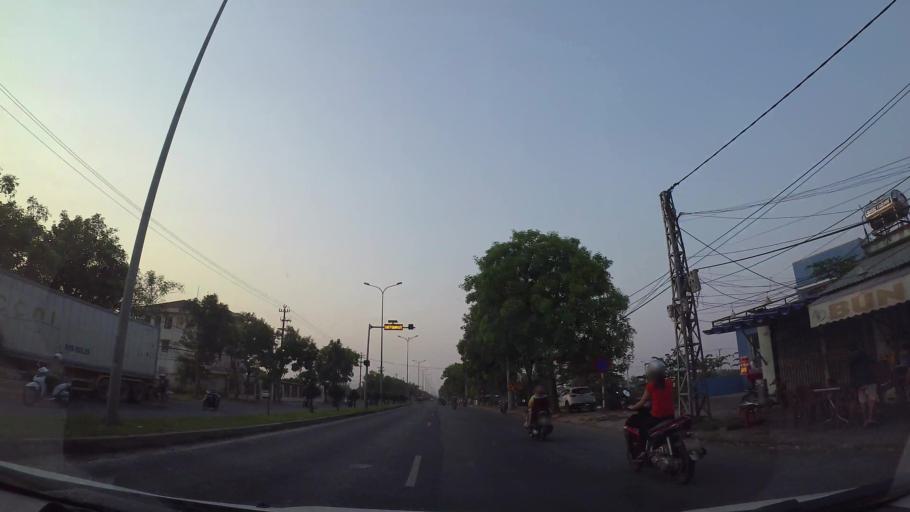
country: VN
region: Da Nang
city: Cam Le
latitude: 15.9517
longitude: 108.2183
